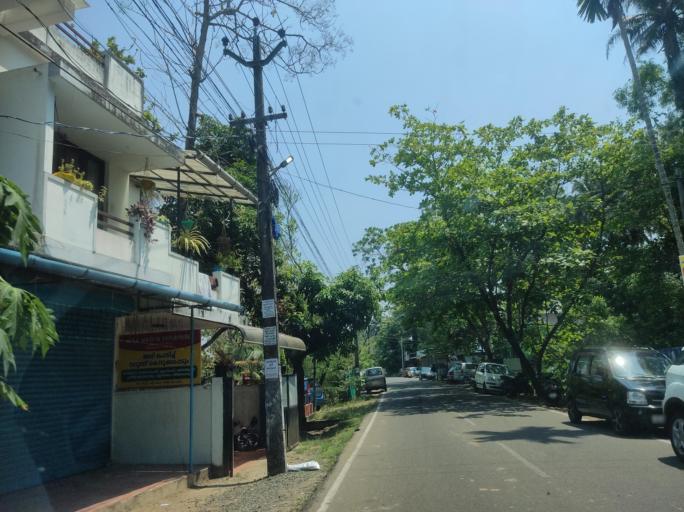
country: IN
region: Kerala
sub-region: Alappuzha
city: Arukutti
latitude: 9.8477
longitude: 76.2950
